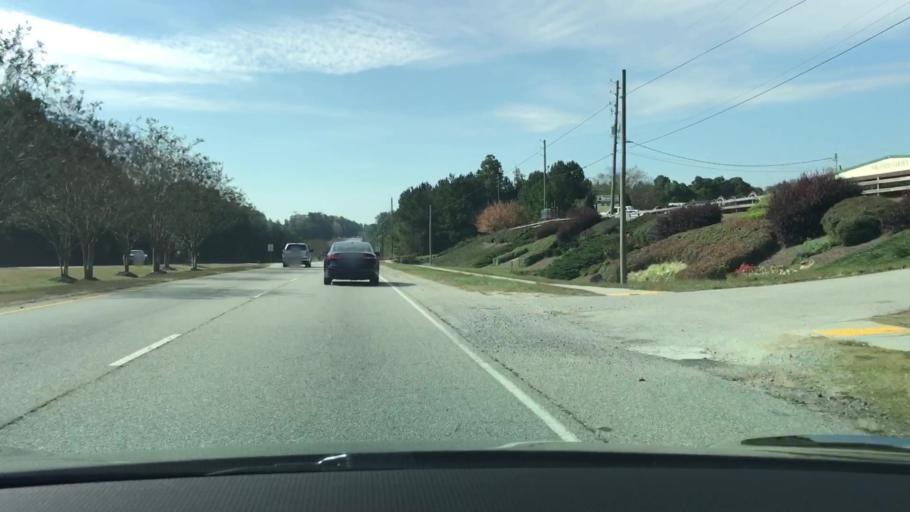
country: US
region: Georgia
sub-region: Gwinnett County
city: Sugar Hill
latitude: 34.0974
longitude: -84.0382
